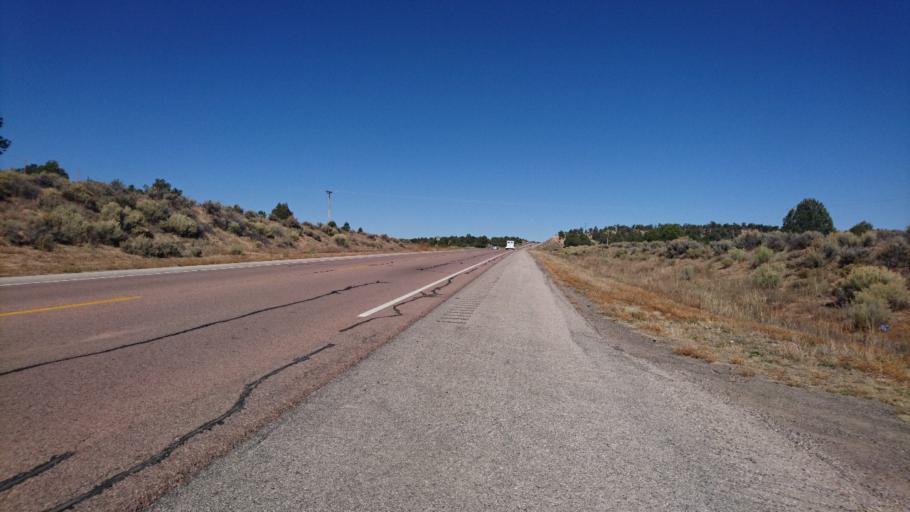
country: US
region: New Mexico
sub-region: McKinley County
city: Black Rock
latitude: 35.3000
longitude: -108.7571
